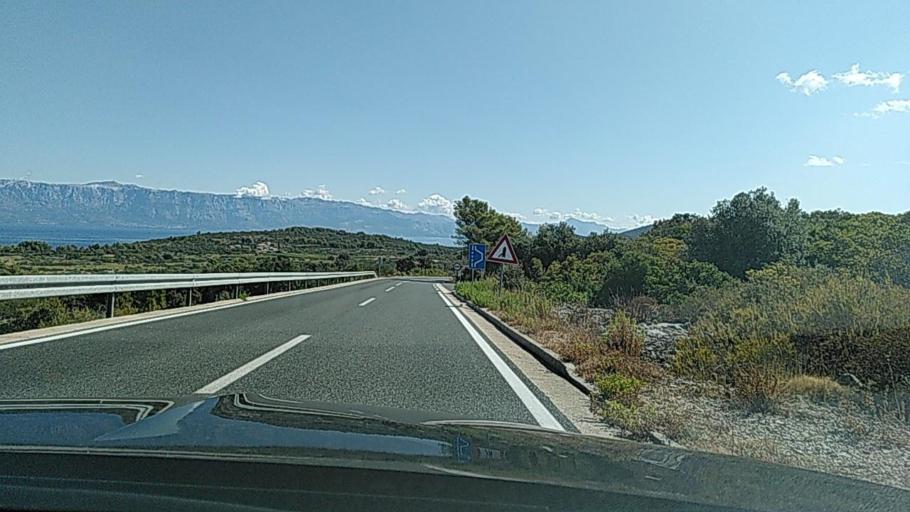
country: HR
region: Splitsko-Dalmatinska
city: Jelsa
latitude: 43.1476
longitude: 16.7850
